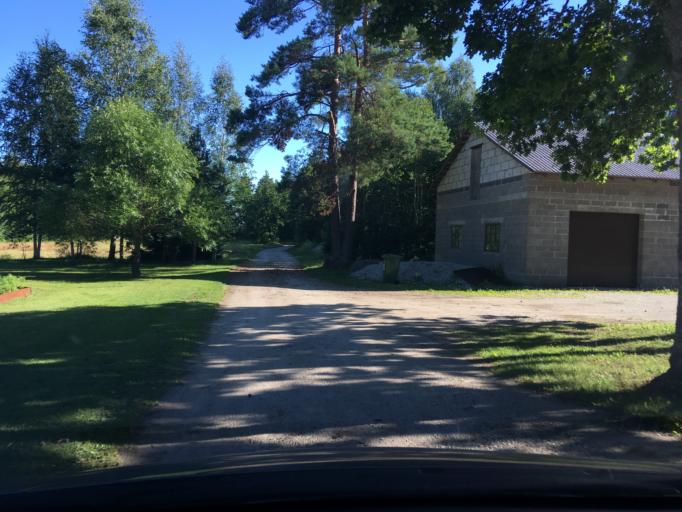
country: EE
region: Laeaene
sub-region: Lihula vald
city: Lihula
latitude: 58.5853
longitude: 23.7363
